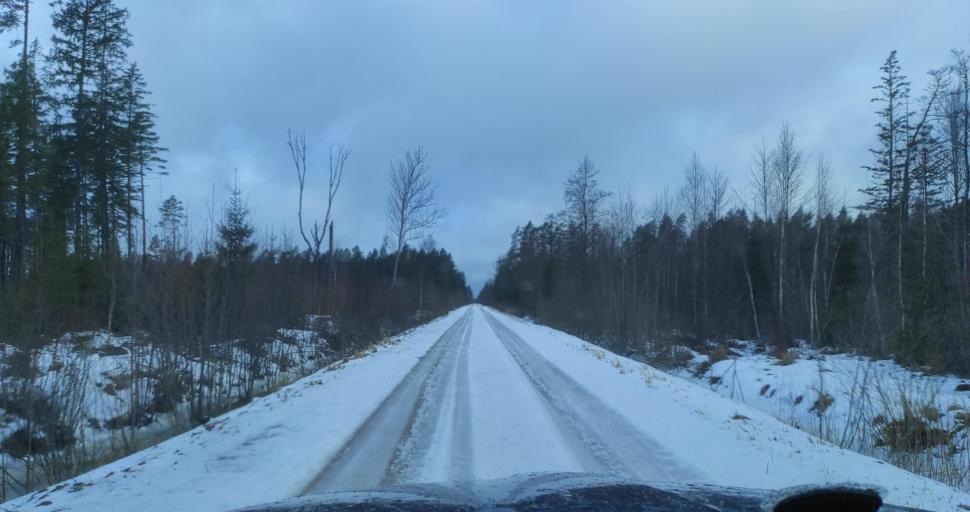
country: LV
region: Dundaga
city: Dundaga
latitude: 57.4058
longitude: 22.0945
